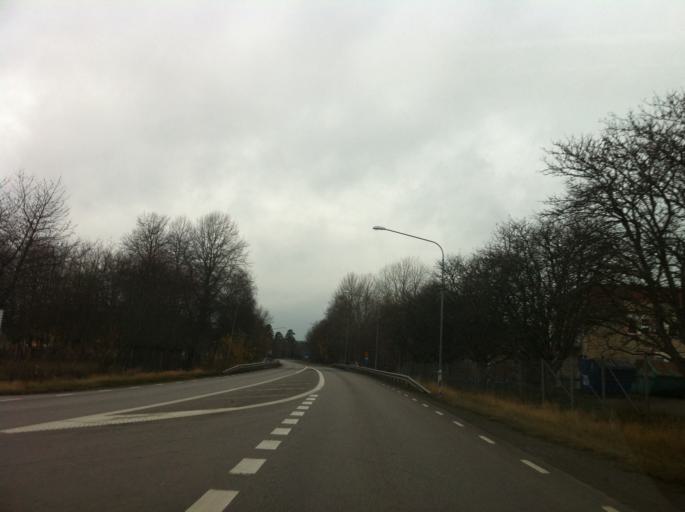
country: SE
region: Joenkoeping
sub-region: Savsjo Kommun
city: Saevsjoe
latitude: 57.3928
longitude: 14.7062
